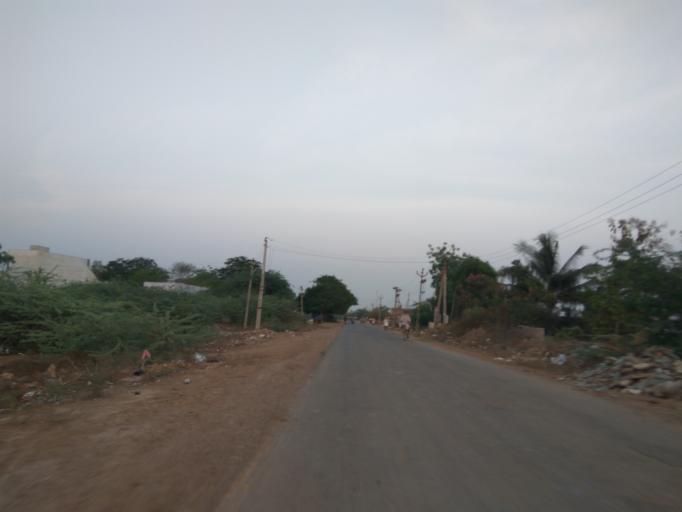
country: IN
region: Andhra Pradesh
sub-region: Prakasam
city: Markapur
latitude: 15.7402
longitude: 79.2522
